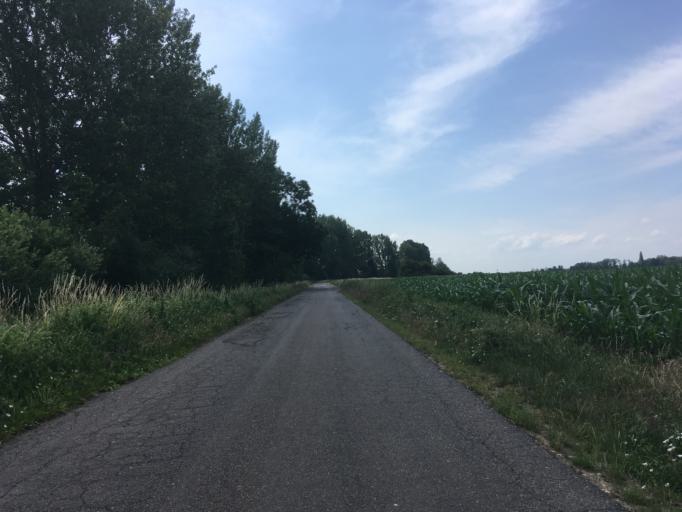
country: DE
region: Saxony-Anhalt
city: Osternienburg
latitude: 51.7599
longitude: 12.0635
